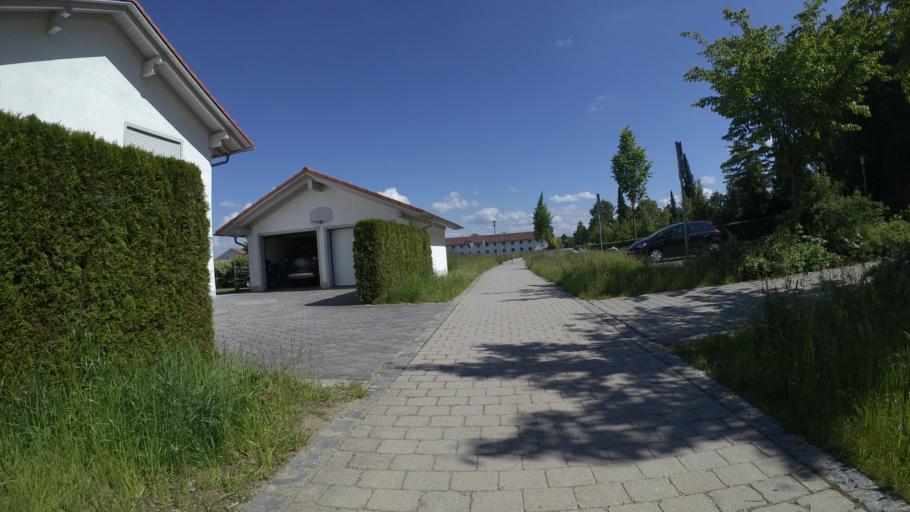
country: DE
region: Bavaria
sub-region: Upper Bavaria
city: Traunreut
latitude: 47.9428
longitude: 12.6028
